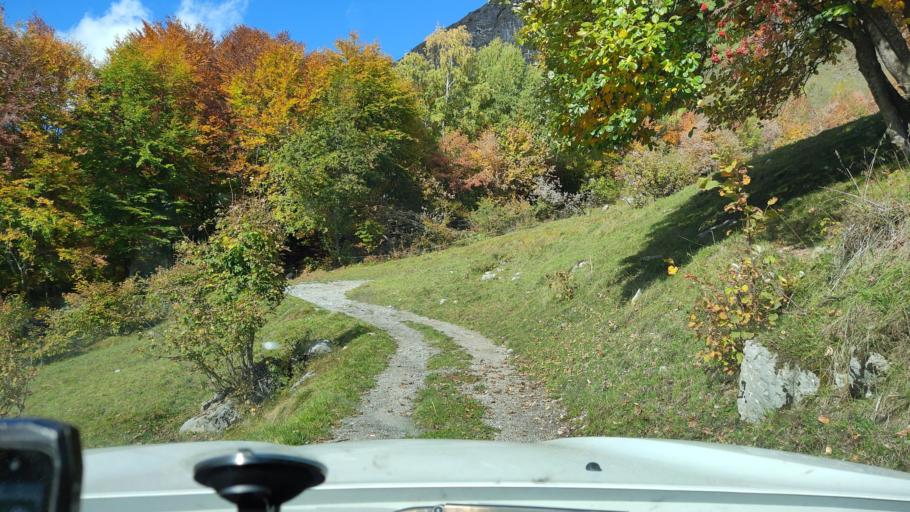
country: FR
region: Rhone-Alpes
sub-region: Departement de la Haute-Savoie
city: La Clusaz
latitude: 45.8723
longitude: 6.4843
